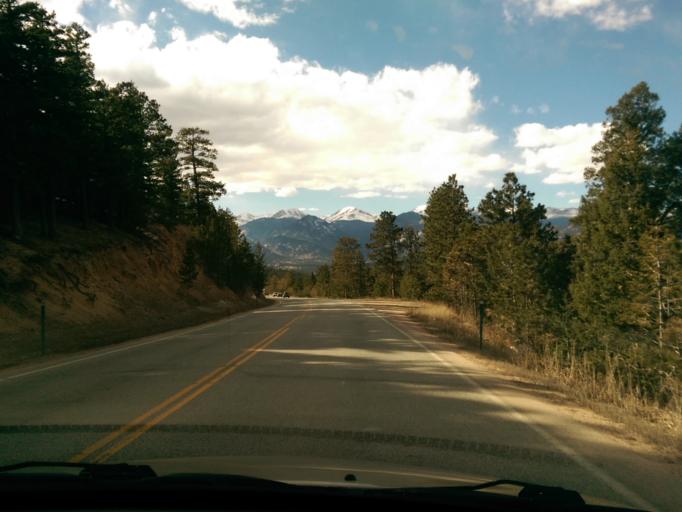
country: US
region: Colorado
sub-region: Larimer County
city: Estes Park
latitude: 40.3598
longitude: -105.4607
